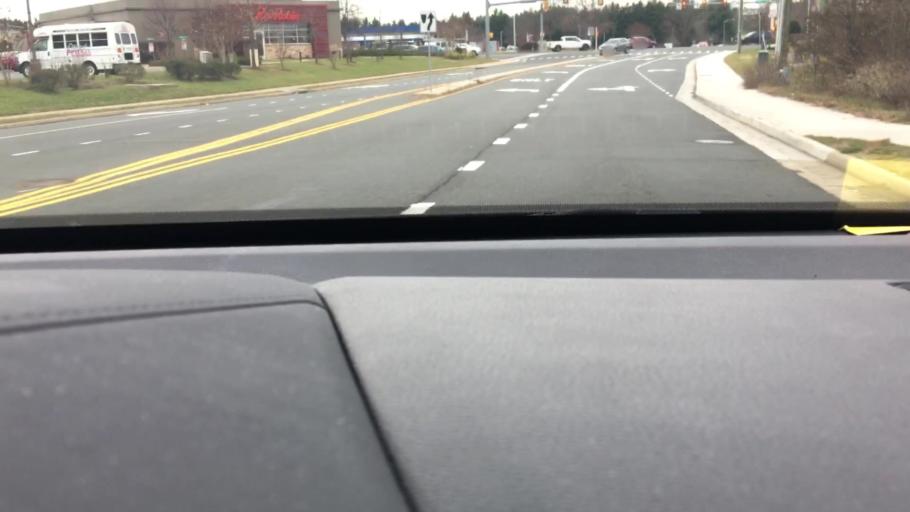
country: US
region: Virginia
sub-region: Prince William County
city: Buckhall
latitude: 38.7487
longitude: -77.4482
